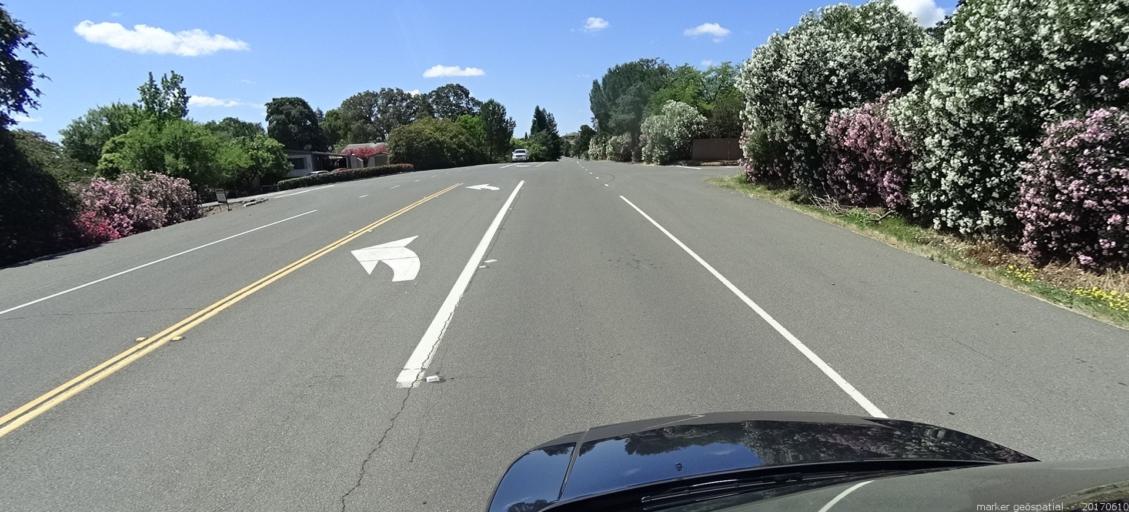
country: US
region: California
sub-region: Butte County
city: Oroville East
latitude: 39.5236
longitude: -121.4666
